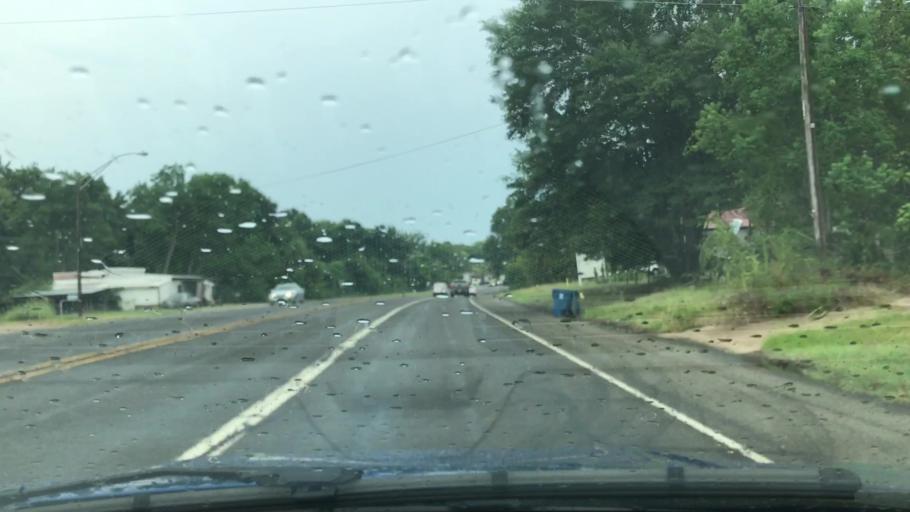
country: US
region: Texas
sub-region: Harrison County
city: Waskom
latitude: 32.4776
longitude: -94.0552
